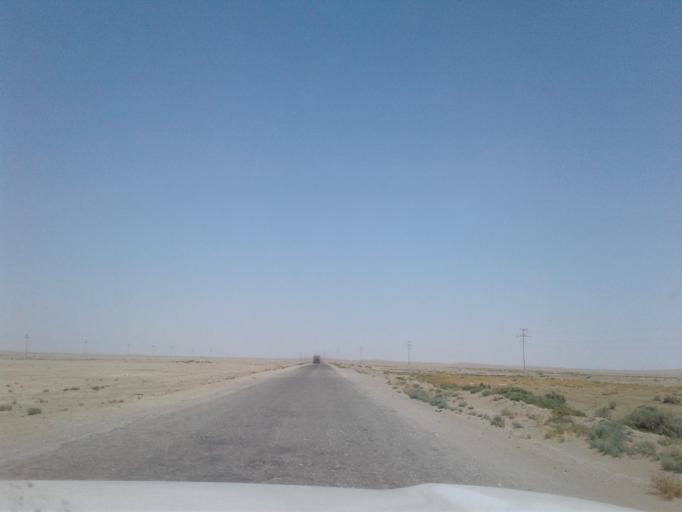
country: TM
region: Balkan
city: Gumdag
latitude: 38.3563
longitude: 54.3758
